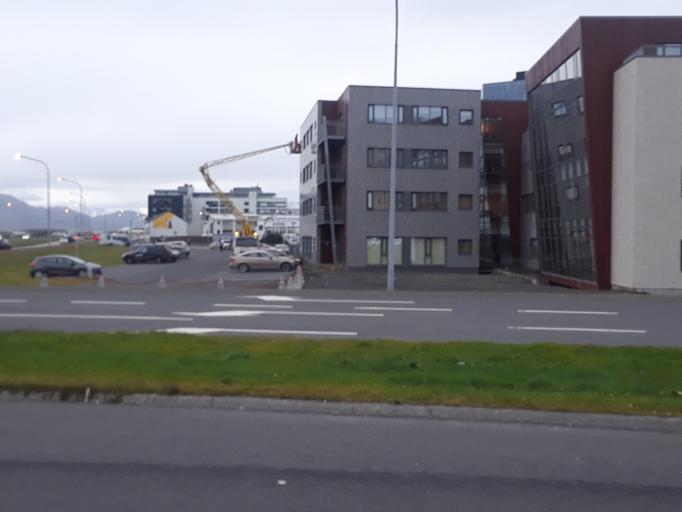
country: IS
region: Capital Region
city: Reykjavik
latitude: 64.1453
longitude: -21.9149
